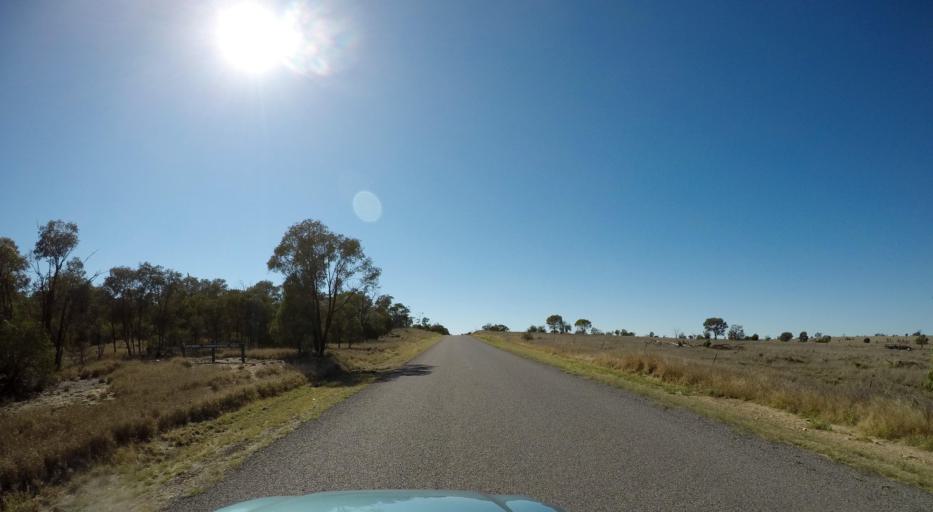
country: AU
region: Queensland
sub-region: Banana
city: Taroom
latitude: -25.7886
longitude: 149.6777
